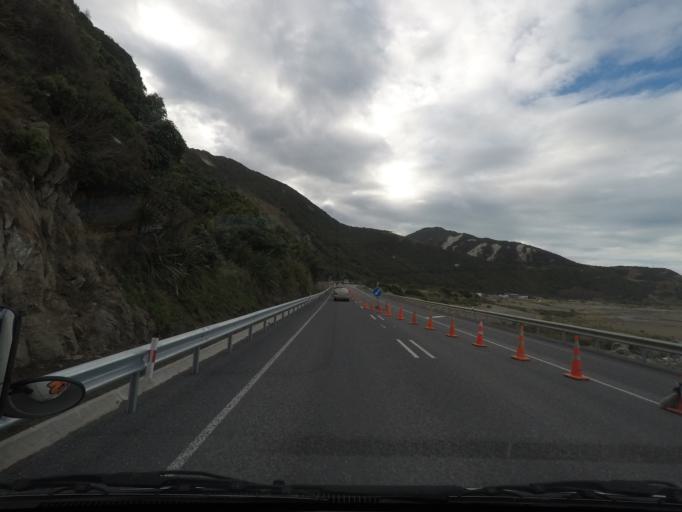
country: NZ
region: Canterbury
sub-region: Kaikoura District
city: Kaikoura
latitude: -42.2204
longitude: 173.8570
